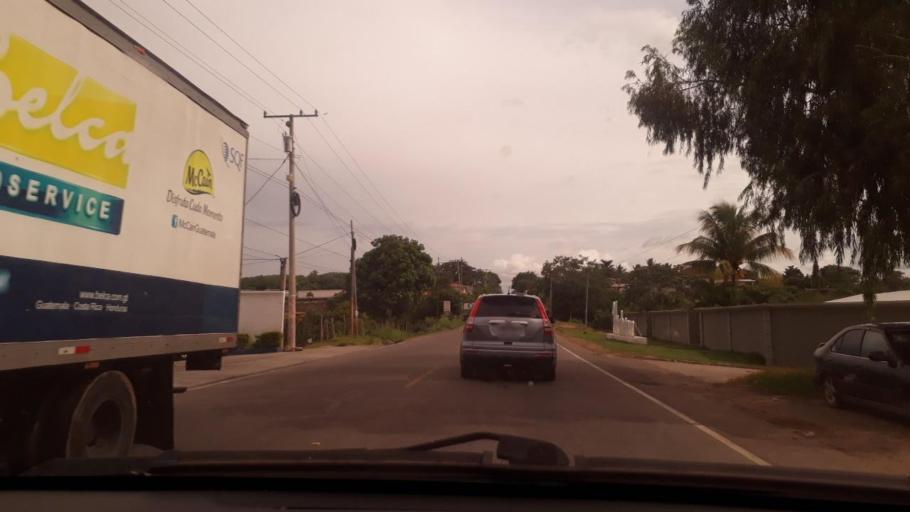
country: GT
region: Jutiapa
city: Jutiapa
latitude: 14.3105
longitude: -89.8682
